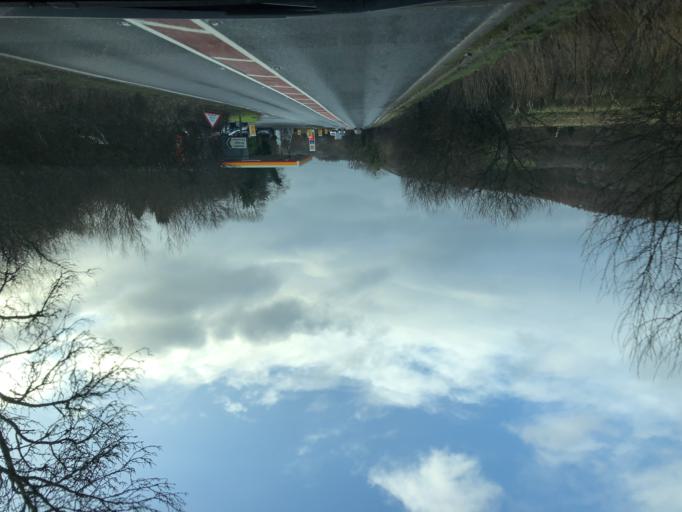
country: GB
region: England
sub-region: Cumbria
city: Grange-over-Sands
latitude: 54.2634
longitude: -2.9622
